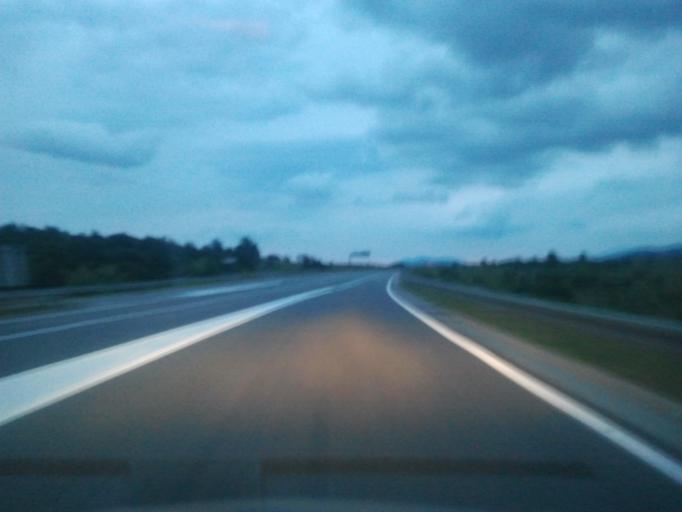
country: HR
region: Zadarska
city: Gracac
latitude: 44.5096
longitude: 15.7459
